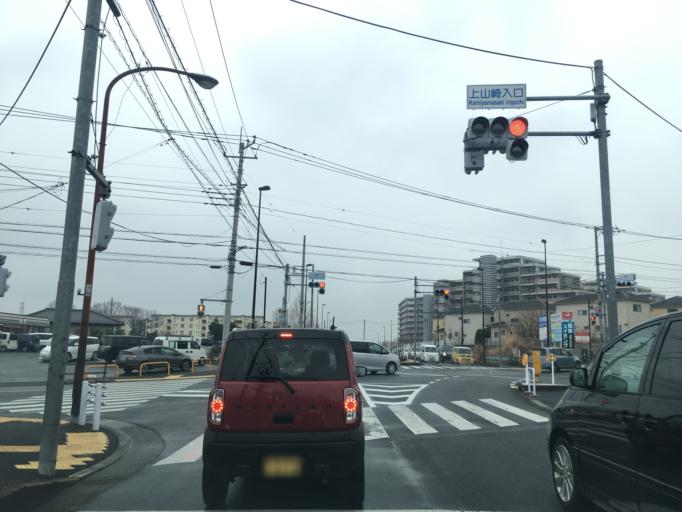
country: JP
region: Tokyo
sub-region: Machida-shi
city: Machida
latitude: 35.5713
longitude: 139.4280
